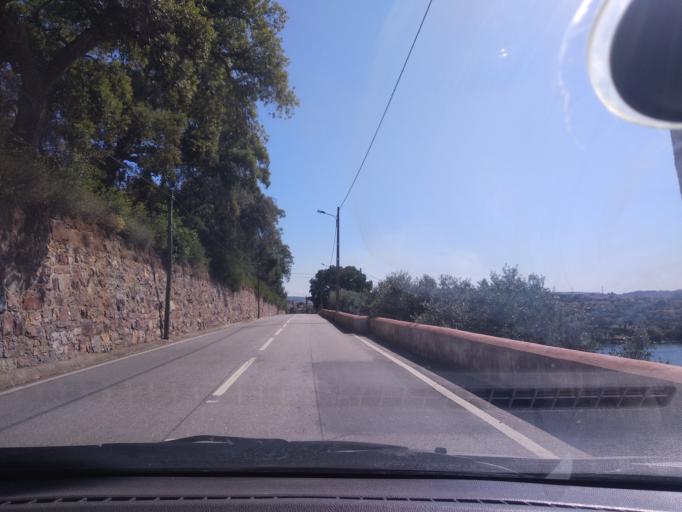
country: PT
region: Portalegre
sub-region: Nisa
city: Nisa
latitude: 39.6490
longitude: -7.6754
